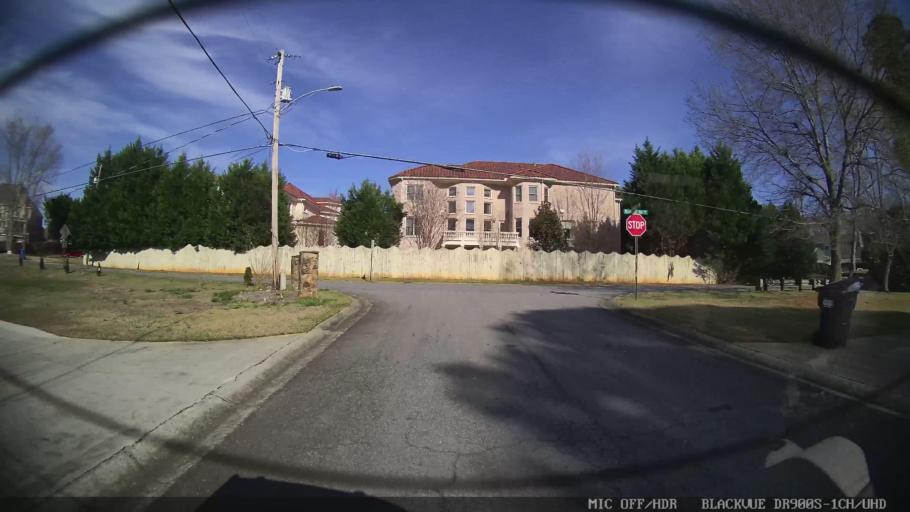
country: US
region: Georgia
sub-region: Cobb County
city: Marietta
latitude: 33.9775
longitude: -84.4877
